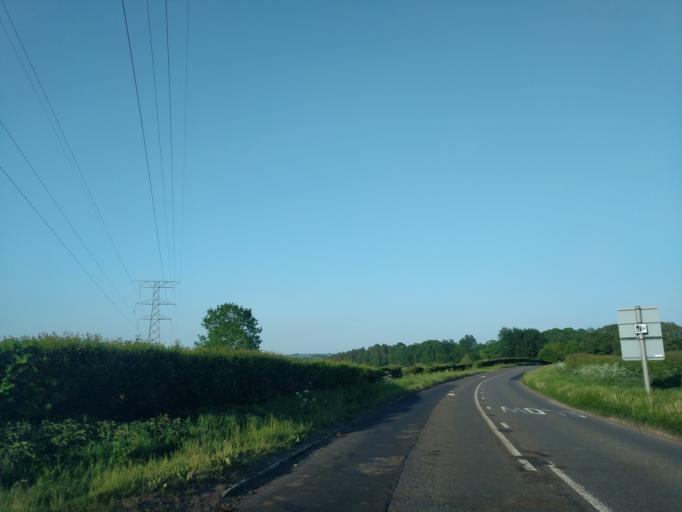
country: GB
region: England
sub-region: Staffordshire
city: Barlaston
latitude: 52.9201
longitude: -2.1864
